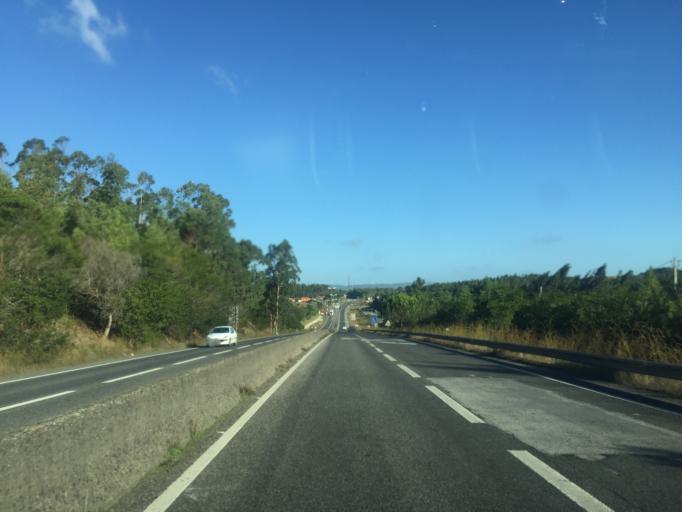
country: PT
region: Santarem
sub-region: Rio Maior
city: Rio Maior
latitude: 39.2766
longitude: -8.9409
